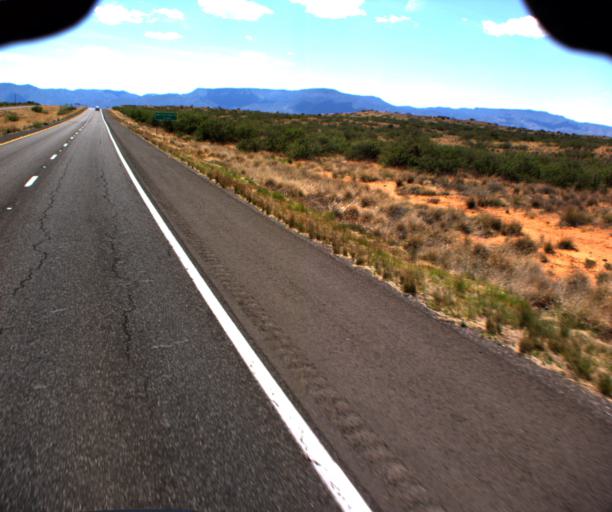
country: US
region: Arizona
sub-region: Yavapai County
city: Cornville
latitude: 34.7744
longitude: -111.9317
